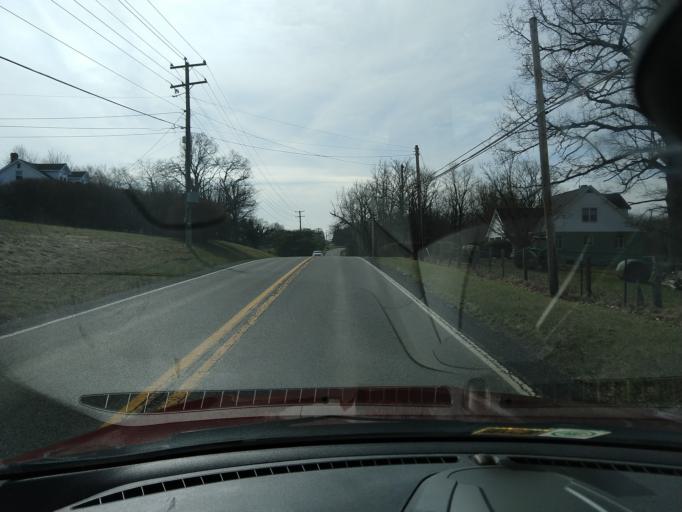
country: US
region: West Virginia
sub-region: Greenbrier County
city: Lewisburg
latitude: 37.8724
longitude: -80.4117
